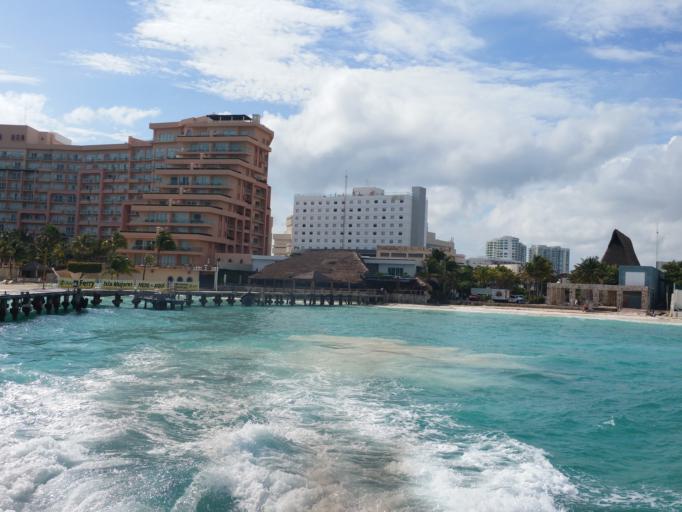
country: MX
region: Quintana Roo
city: Isla Mujeres
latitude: 21.1380
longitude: -86.7462
